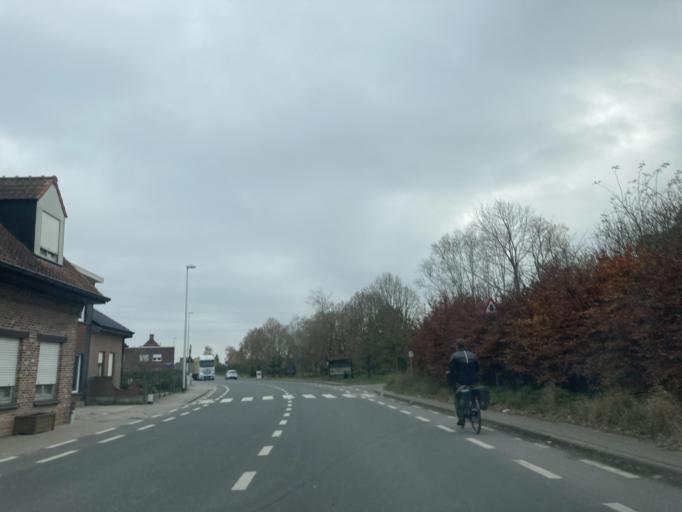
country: BE
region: Flanders
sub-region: Provincie West-Vlaanderen
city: Lendelede
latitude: 50.8618
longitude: 3.1835
